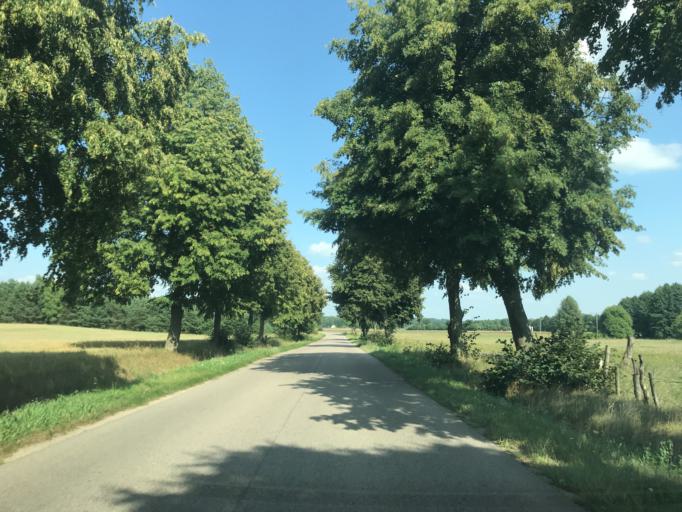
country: PL
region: Warmian-Masurian Voivodeship
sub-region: Powiat dzialdowski
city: Ilowo -Osada
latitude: 53.1083
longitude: 20.2882
